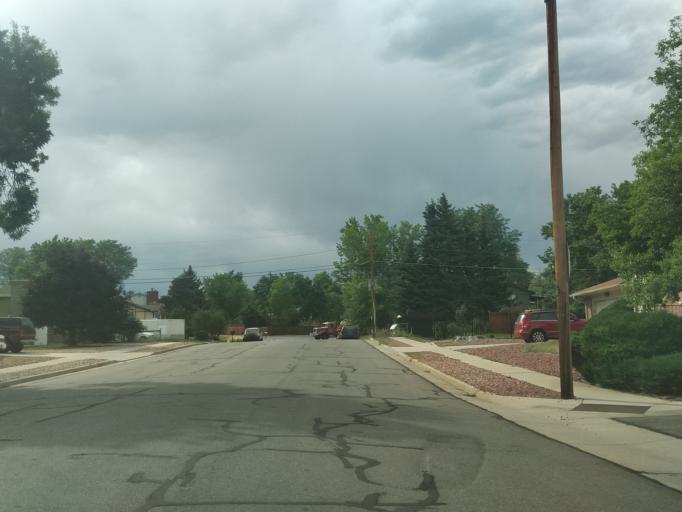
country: US
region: Colorado
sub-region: Jefferson County
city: Lakewood
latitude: 39.6995
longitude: -105.1068
